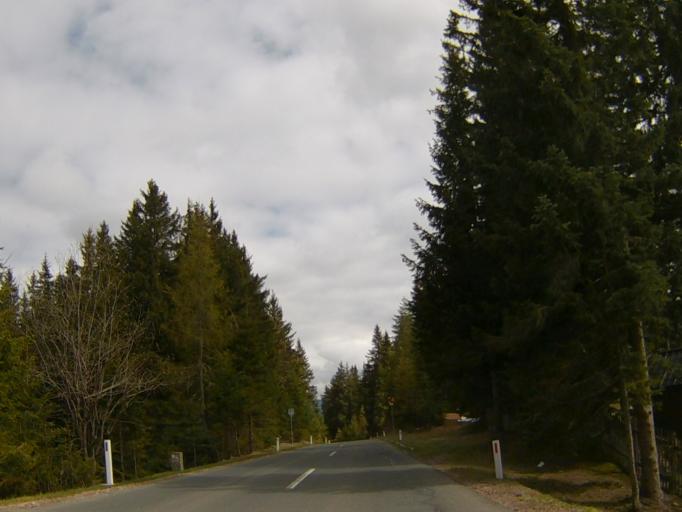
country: AT
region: Carinthia
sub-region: Politischer Bezirk Villach Land
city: Arnoldstein
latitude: 46.5909
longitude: 13.7429
